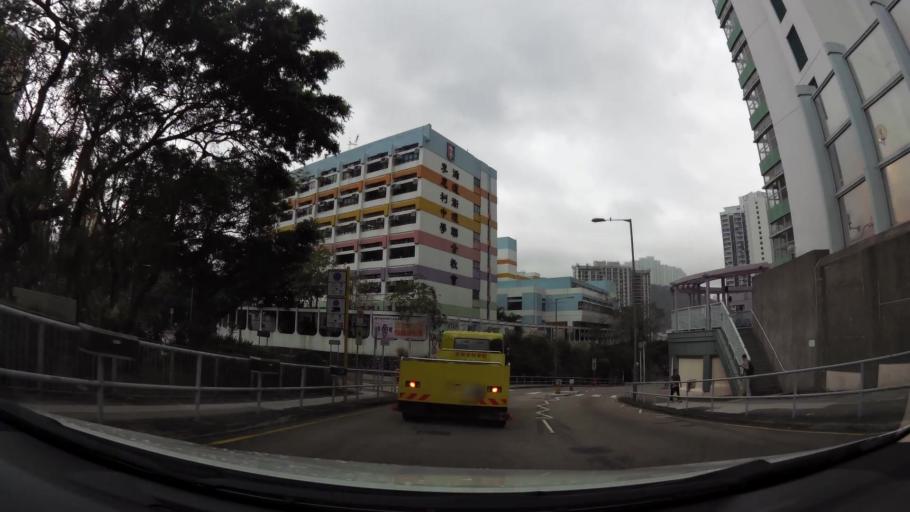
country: HK
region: Tsuen Wan
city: Tsuen Wan
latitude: 22.3657
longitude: 114.1271
